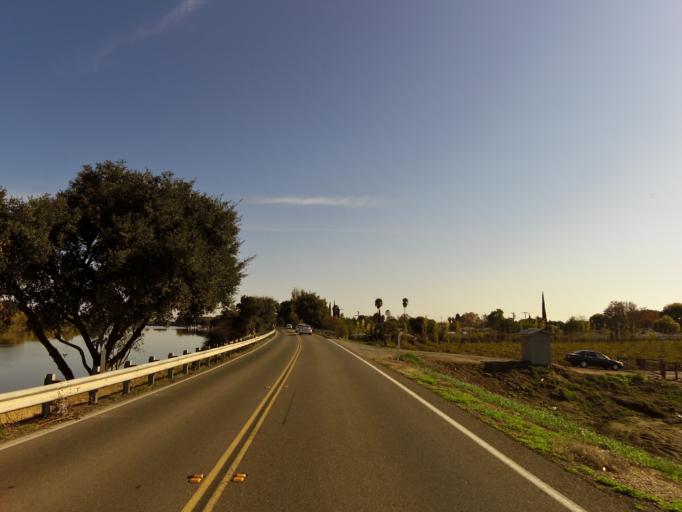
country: US
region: California
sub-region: Solano County
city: Rio Vista
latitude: 38.1630
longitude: -121.6186
